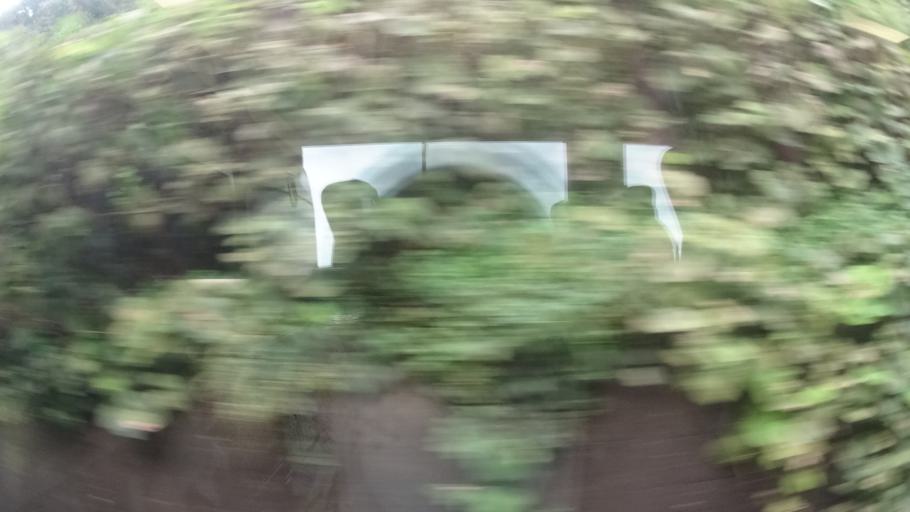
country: JP
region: Niigata
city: Murakami
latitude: 38.5482
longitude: 139.5504
